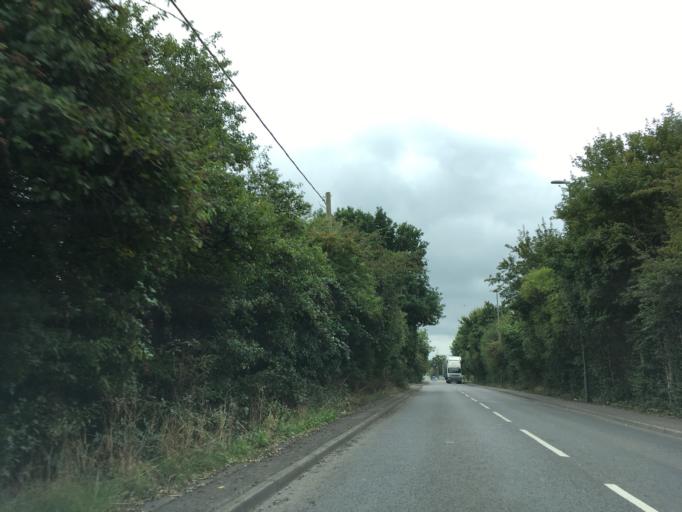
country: GB
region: England
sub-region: South Gloucestershire
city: Siston
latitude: 51.4521
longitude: -2.4633
